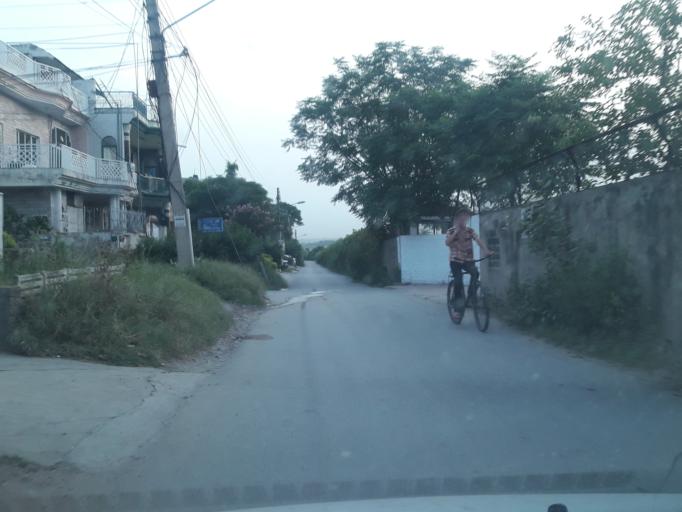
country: PK
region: Punjab
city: Rawalpindi
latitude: 33.6750
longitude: 73.1401
